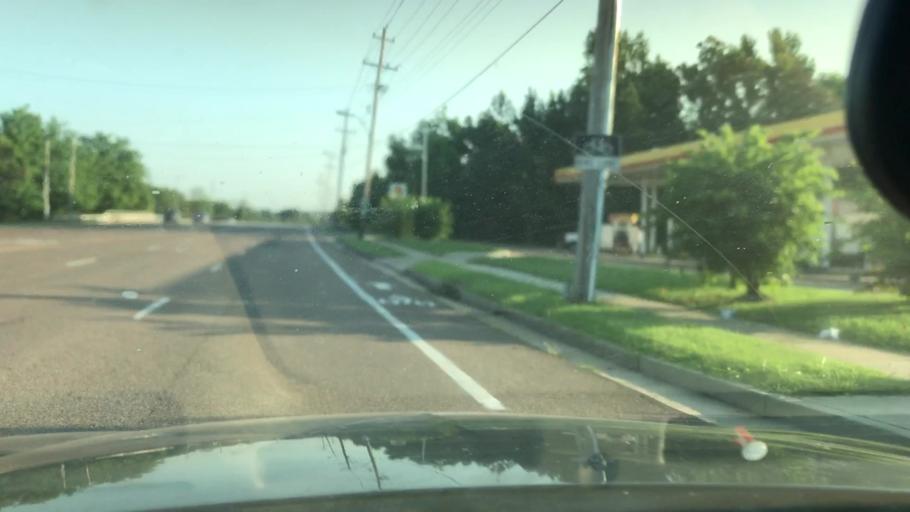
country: US
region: Tennessee
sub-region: Shelby County
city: Bartlett
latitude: 35.1890
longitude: -89.8140
